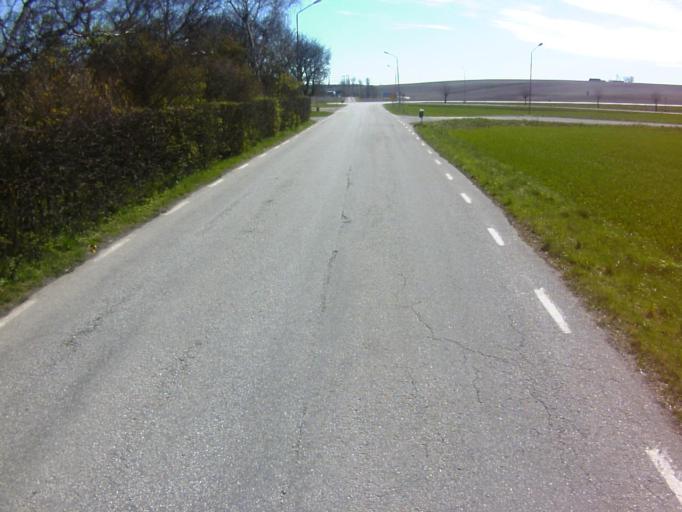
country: SE
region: Skane
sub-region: Kavlinge Kommun
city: Hofterup
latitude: 55.7675
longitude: 12.9556
